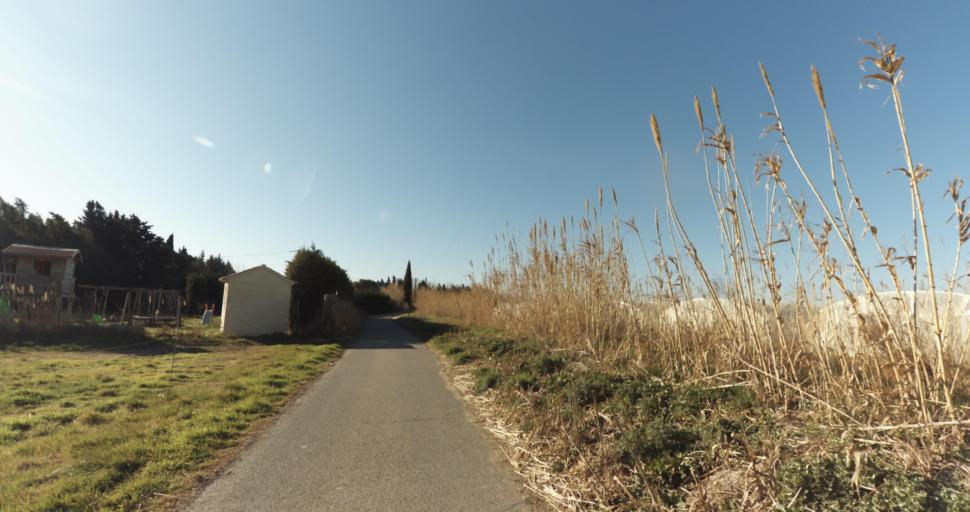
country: FR
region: Provence-Alpes-Cote d'Azur
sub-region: Departement des Bouches-du-Rhone
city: Rognonas
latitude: 43.9119
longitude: 4.7826
